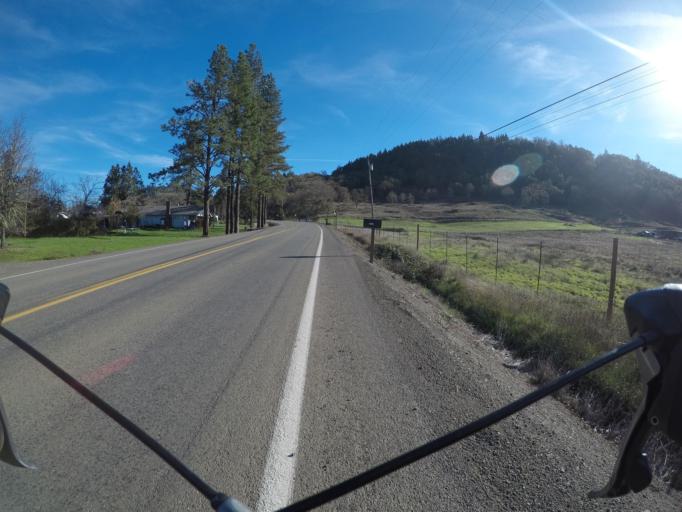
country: US
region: Oregon
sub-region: Douglas County
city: Winston
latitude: 43.1860
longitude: -123.4609
